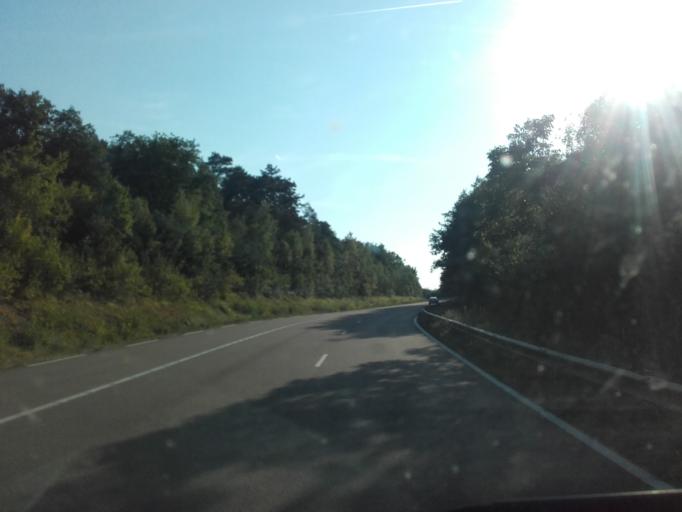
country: FR
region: Bourgogne
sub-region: Departement de l'Yonne
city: Venoy
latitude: 47.8123
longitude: 3.7004
